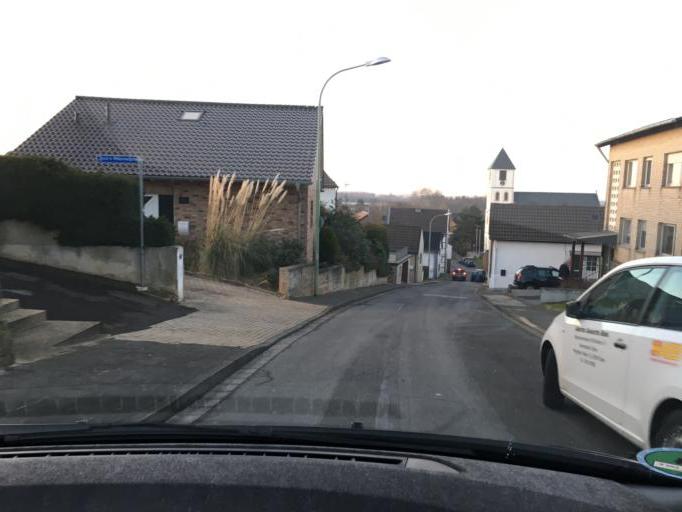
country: DE
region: North Rhine-Westphalia
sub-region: Regierungsbezirk Koln
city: Kreuzau
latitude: 50.7700
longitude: 6.4463
